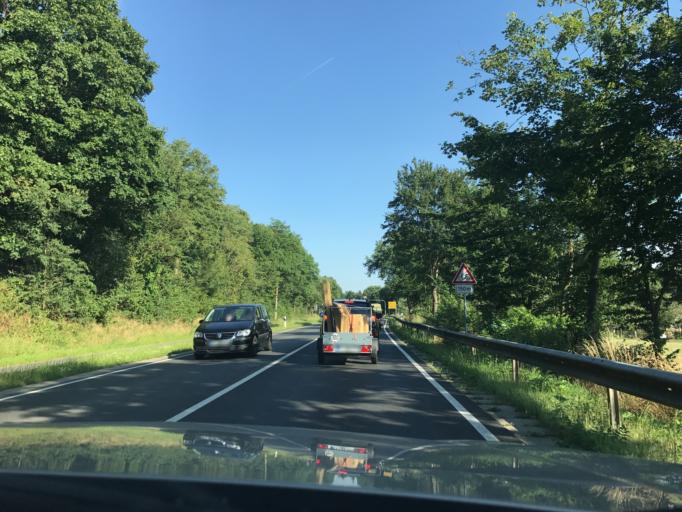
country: DE
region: North Rhine-Westphalia
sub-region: Regierungsbezirk Dusseldorf
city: Rheurdt
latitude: 51.4109
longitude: 6.4823
